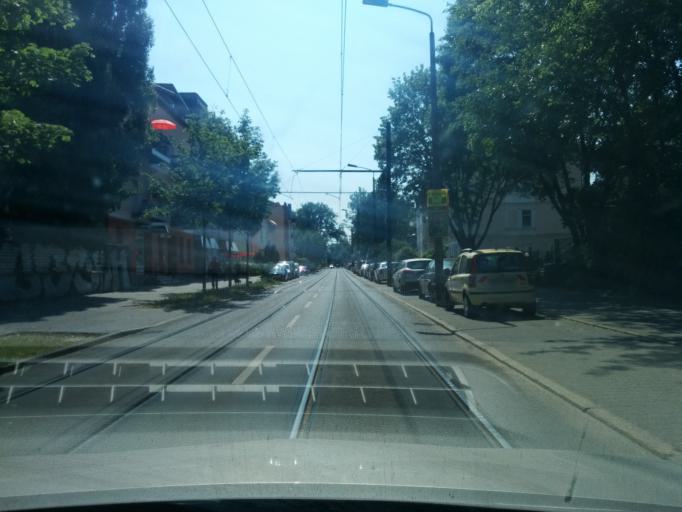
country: DE
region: Berlin
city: Grunau
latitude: 52.4199
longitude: 13.5783
